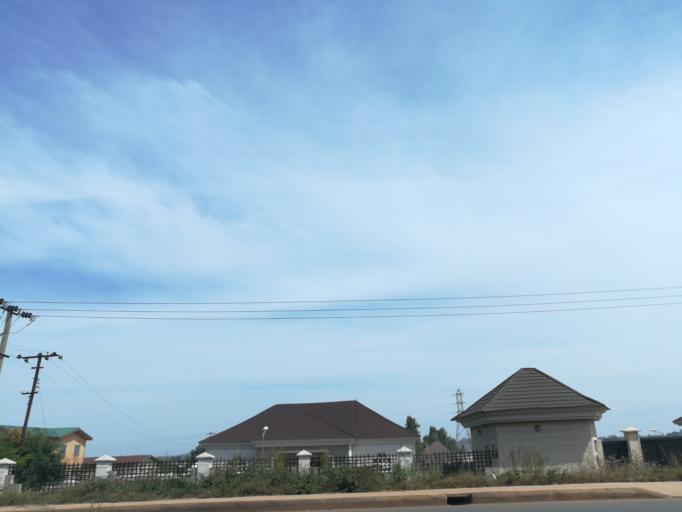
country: NG
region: Plateau
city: Bukuru
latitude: 9.7740
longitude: 8.8605
